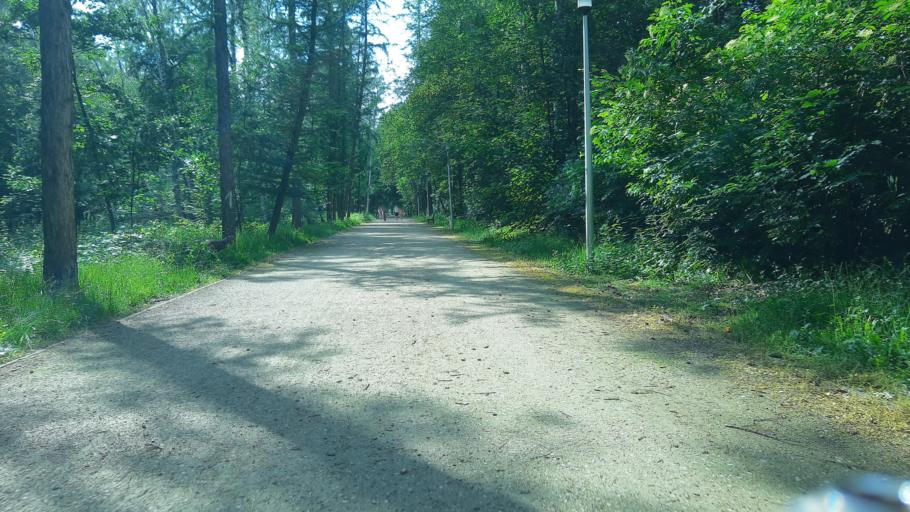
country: PL
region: Lodz Voivodeship
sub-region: Powiat sieradzki
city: Sieradz
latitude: 51.5965
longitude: 18.7580
